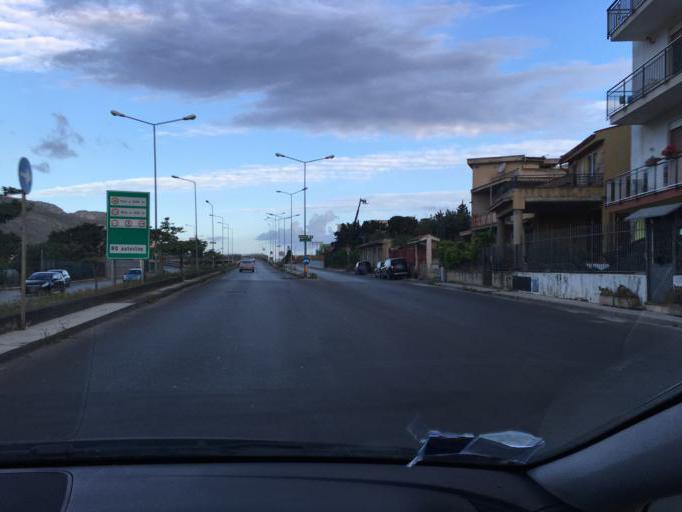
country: IT
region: Sicily
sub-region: Palermo
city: Isola delle Femmine
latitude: 38.1916
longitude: 13.2900
